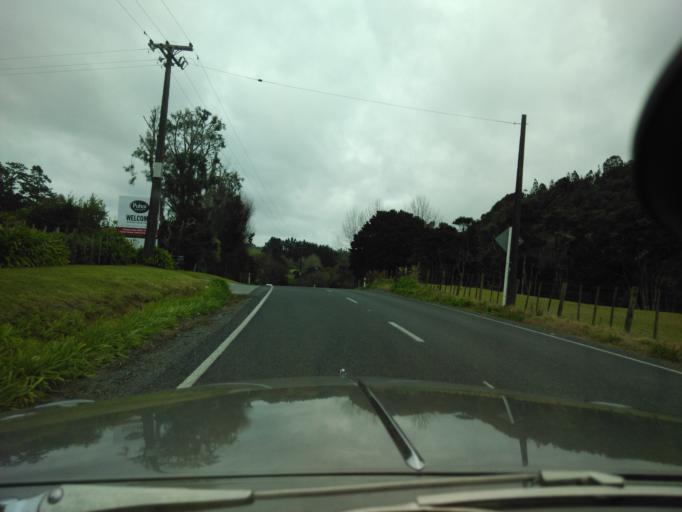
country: NZ
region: Auckland
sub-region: Auckland
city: Warkworth
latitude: -36.5039
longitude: 174.6381
